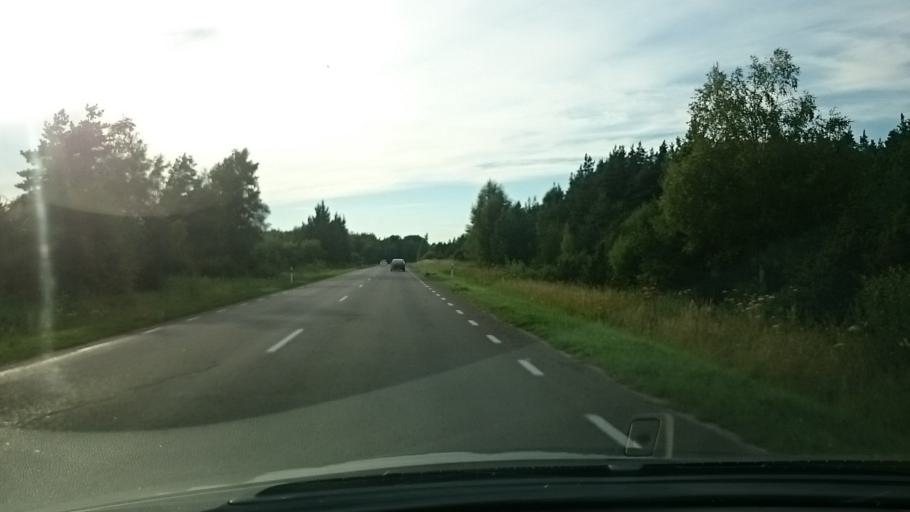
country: EE
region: Saare
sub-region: Kuressaare linn
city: Kuressaare
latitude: 58.2770
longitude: 22.4417
